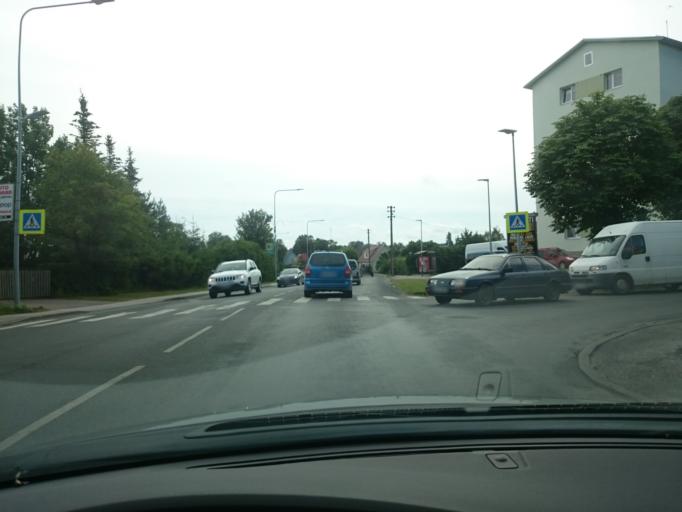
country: EE
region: Laeaene
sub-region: Haapsalu linn
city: Haapsalu
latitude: 58.9391
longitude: 23.5453
